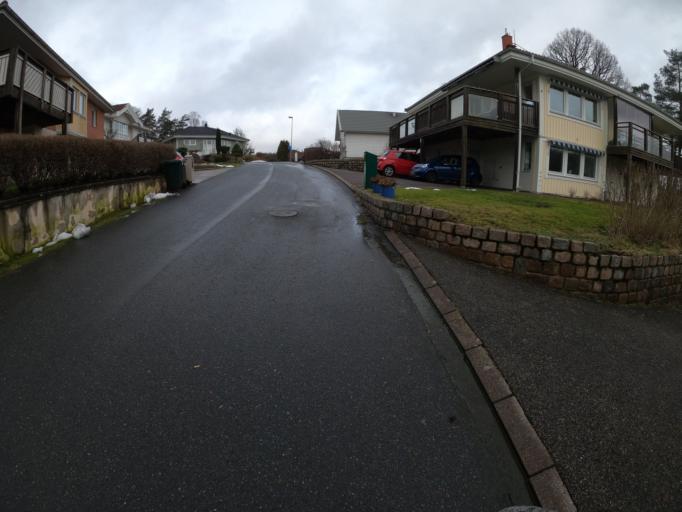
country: SE
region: Vaestra Goetaland
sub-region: Harryda Kommun
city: Molnlycke
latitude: 57.6448
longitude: 12.1046
